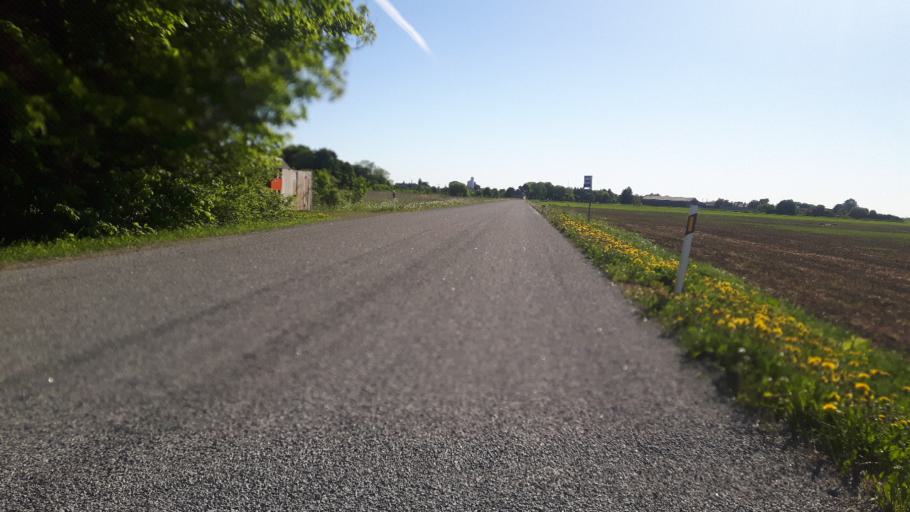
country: EE
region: Ida-Virumaa
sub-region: Kohtla-Jaerve linn
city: Kohtla-Jarve
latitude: 59.4363
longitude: 27.2578
